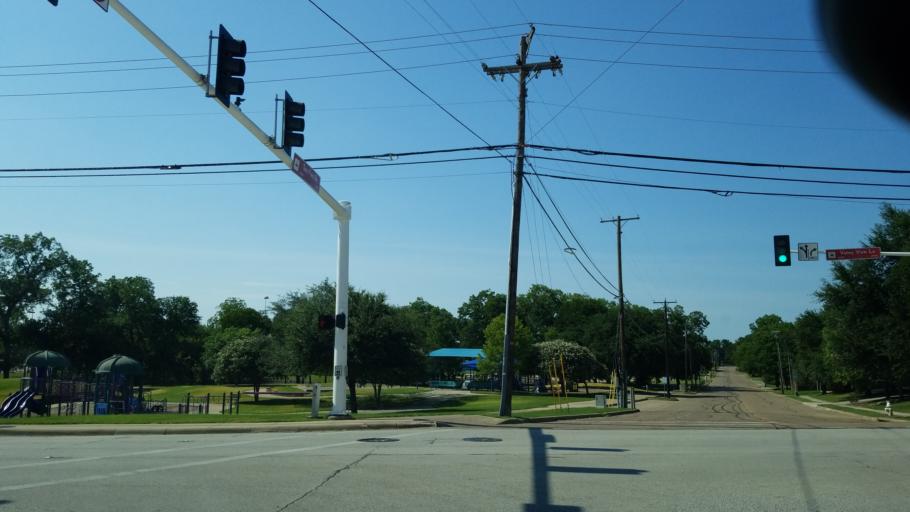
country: US
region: Texas
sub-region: Dallas County
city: Farmers Branch
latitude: 32.9242
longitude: -96.8875
